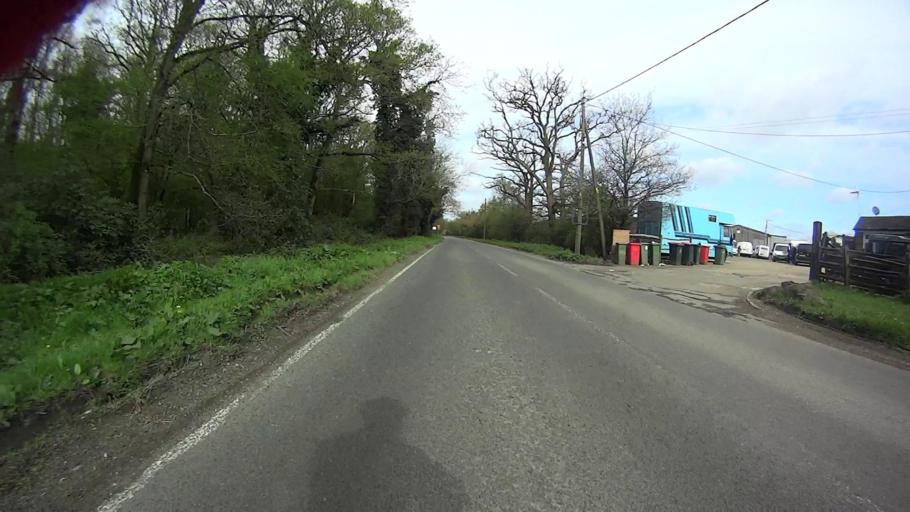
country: GB
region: England
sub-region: West Sussex
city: Langley Green
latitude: 51.1351
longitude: -0.2192
